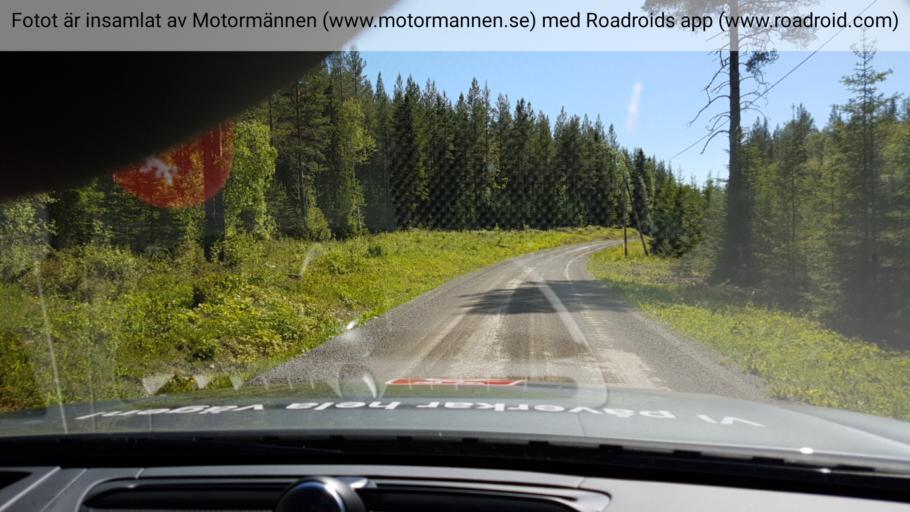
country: SE
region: Jaemtland
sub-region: OEstersunds Kommun
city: Brunflo
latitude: 62.9847
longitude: 14.7111
